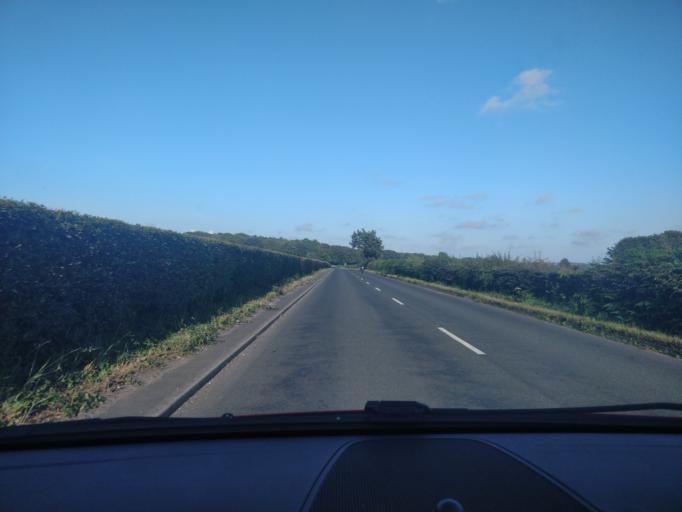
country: GB
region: England
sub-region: Lancashire
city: Tarleton
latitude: 53.6398
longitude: -2.8392
